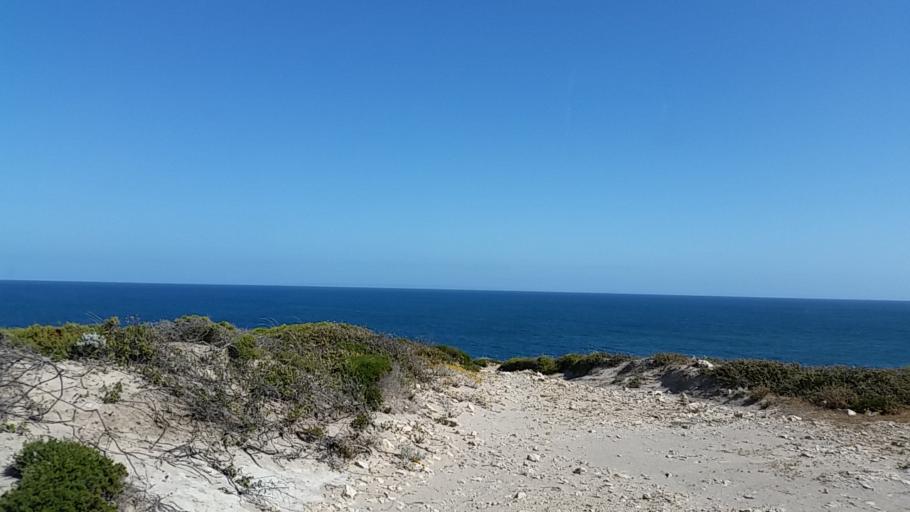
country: AU
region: South Australia
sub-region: Yorke Peninsula
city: Honiton
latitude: -35.2386
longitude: 137.1578
